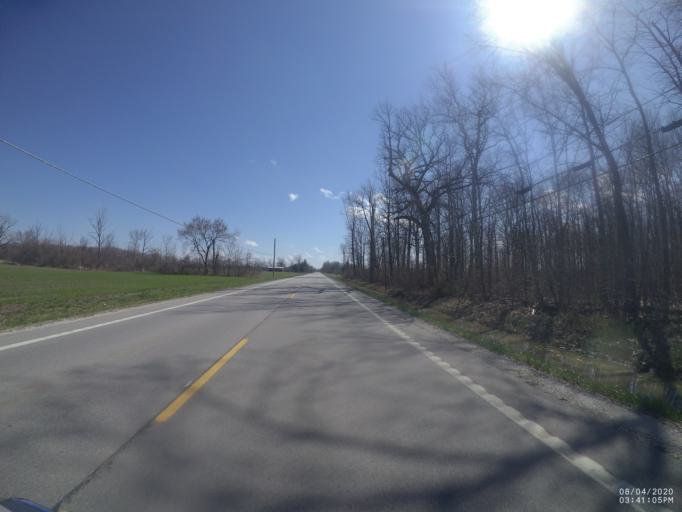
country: US
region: Ohio
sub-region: Sandusky County
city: Stony Prairie
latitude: 41.2660
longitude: -83.2350
